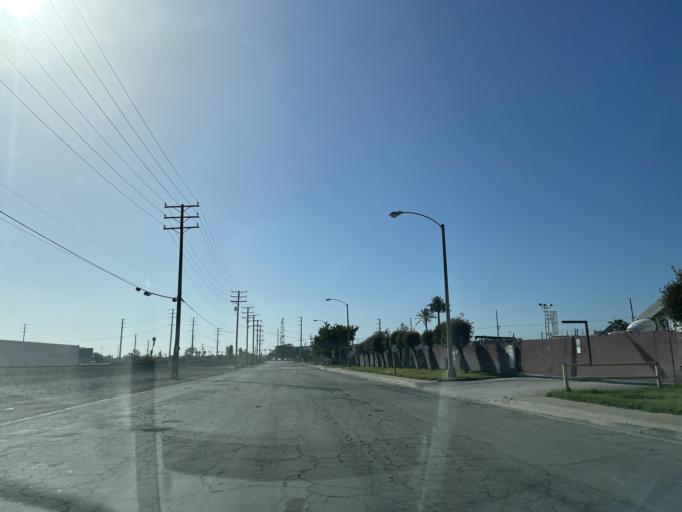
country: US
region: California
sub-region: Los Angeles County
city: La Mirada
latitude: 33.9008
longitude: -118.0342
